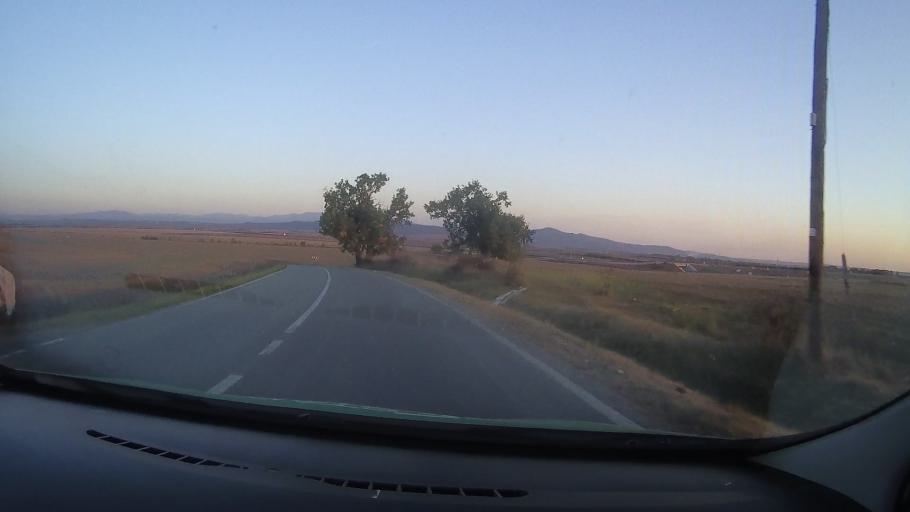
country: RO
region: Timis
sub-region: Comuna Manastiur
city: Manastiur
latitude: 45.8184
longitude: 22.0712
